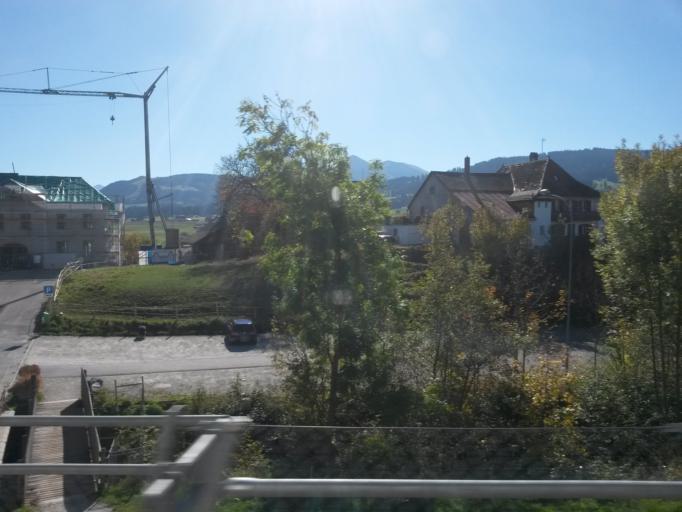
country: CH
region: Fribourg
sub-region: Gruyere District
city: Sales
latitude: 46.6240
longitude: 6.9917
